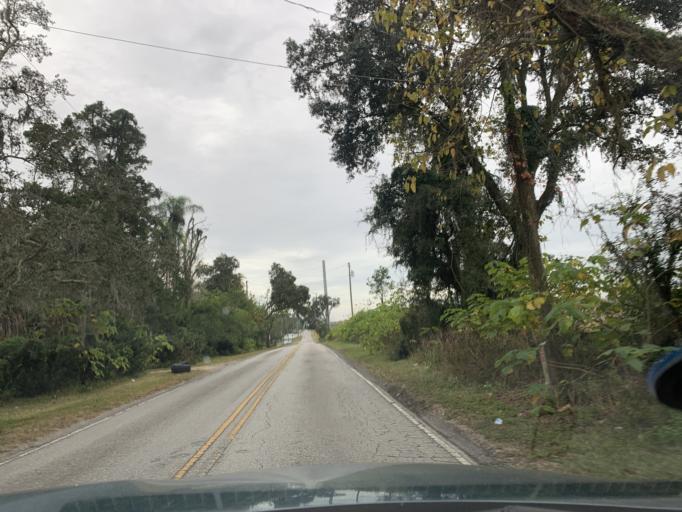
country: US
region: Florida
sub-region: Pasco County
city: Zephyrhills North
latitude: 28.2757
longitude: -82.1798
